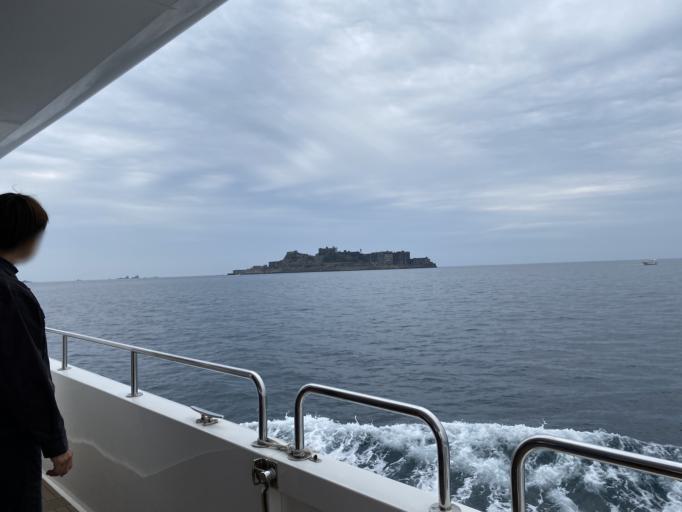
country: JP
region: Nagasaki
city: Nagasaki-shi
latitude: 32.6271
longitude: 129.7498
